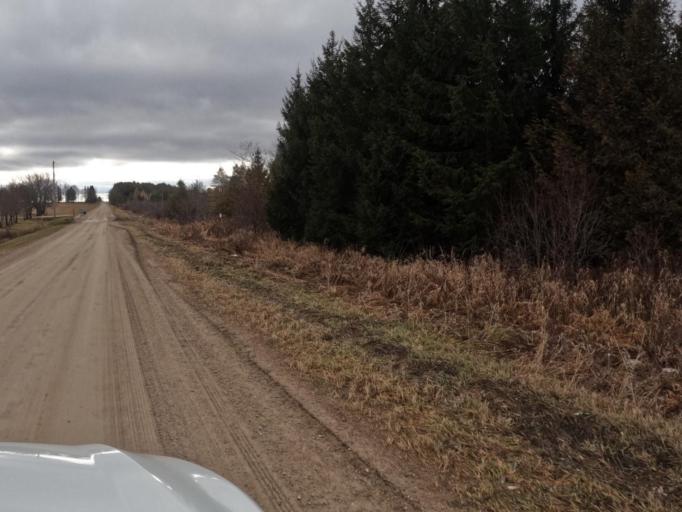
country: CA
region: Ontario
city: Shelburne
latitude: 43.9683
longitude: -80.4014
